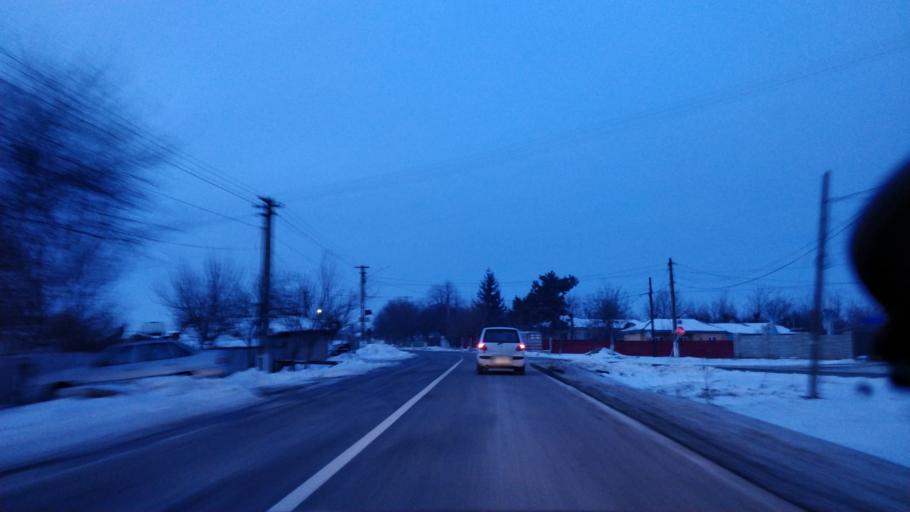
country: RO
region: Vrancea
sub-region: Comuna Nanesti
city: Nanesti
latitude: 45.5332
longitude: 27.4984
